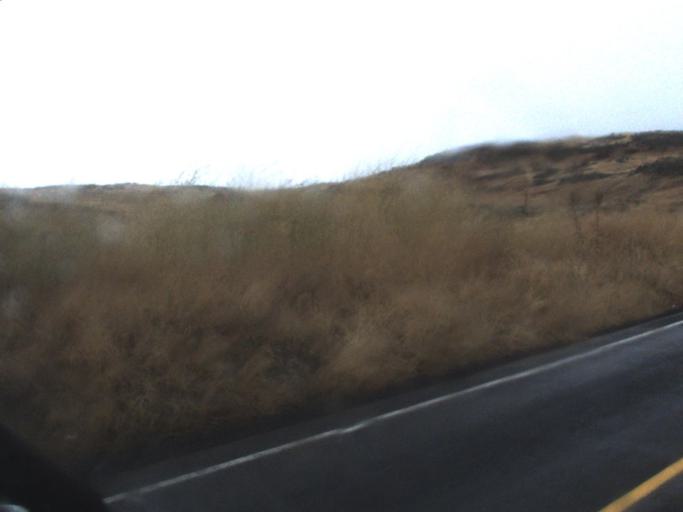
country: US
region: Washington
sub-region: Spokane County
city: Medical Lake
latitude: 47.2473
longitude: -117.9215
